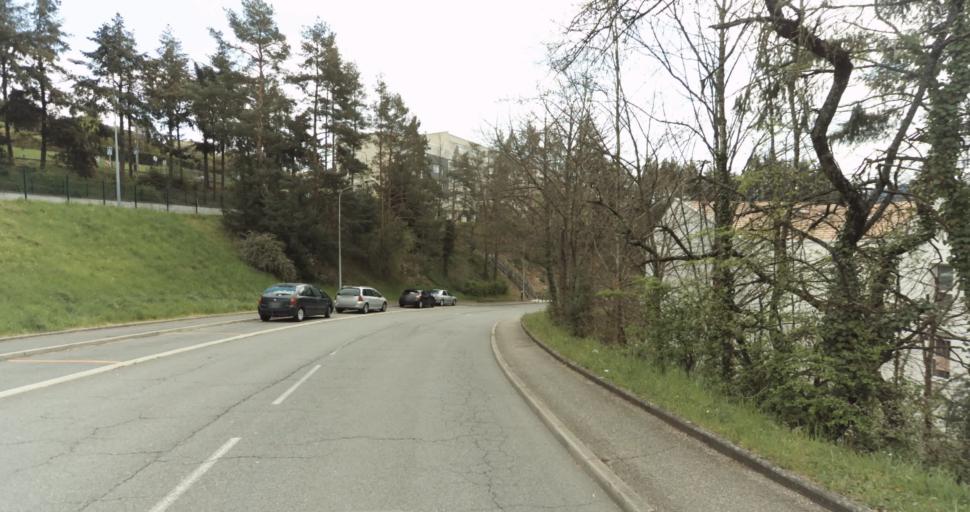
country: FR
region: Rhone-Alpes
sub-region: Departement du Rhone
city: Tarare
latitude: 45.8969
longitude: 4.4439
